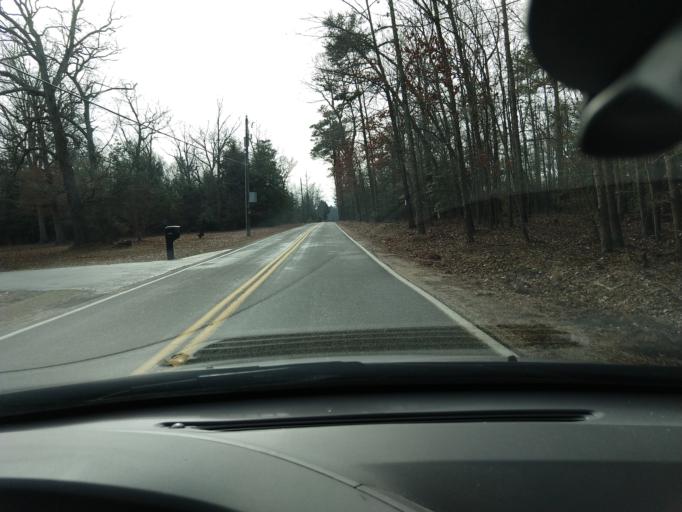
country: US
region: Virginia
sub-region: Henrico County
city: Fort Lee
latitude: 37.4444
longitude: -77.2337
